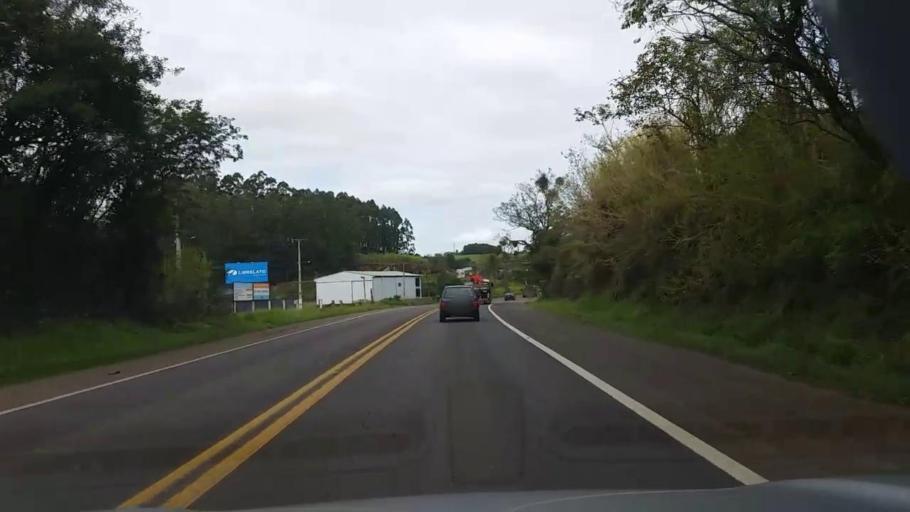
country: BR
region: Rio Grande do Sul
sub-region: Arroio Do Meio
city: Arroio do Meio
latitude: -29.4119
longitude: -52.0272
